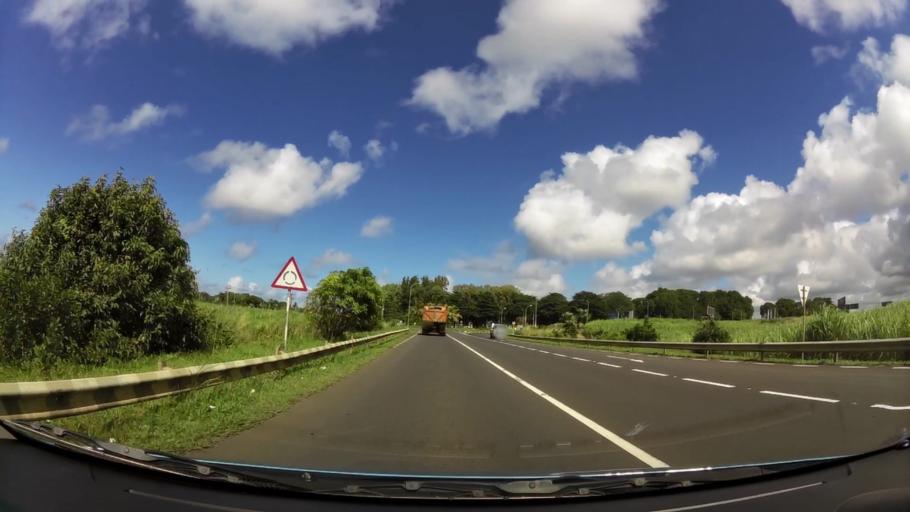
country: MU
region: Grand Port
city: Plaine Magnien
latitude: -20.4226
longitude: 57.6604
